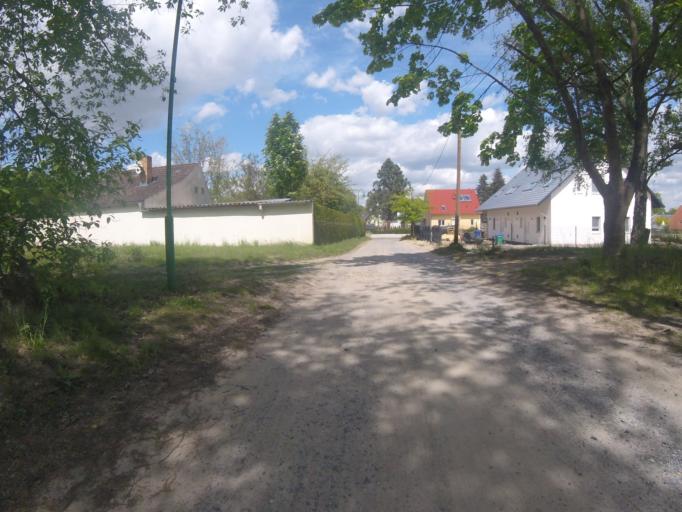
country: DE
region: Brandenburg
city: Bestensee
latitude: 52.2636
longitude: 13.6246
